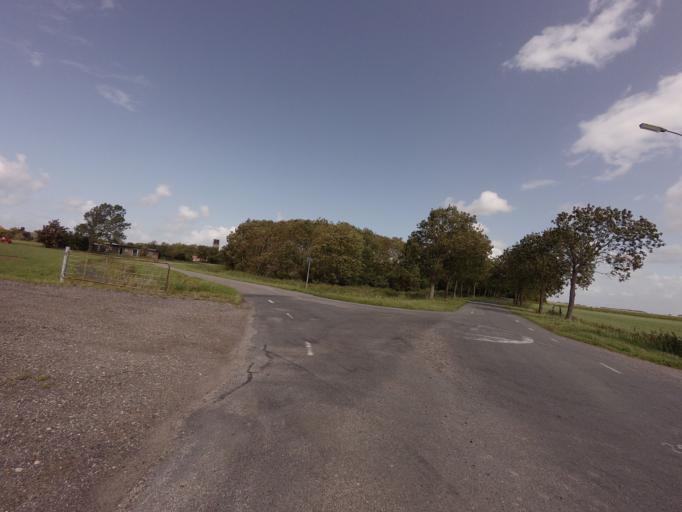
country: NL
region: Friesland
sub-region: Gemeente Harlingen
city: Harlingen
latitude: 53.1120
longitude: 5.4402
